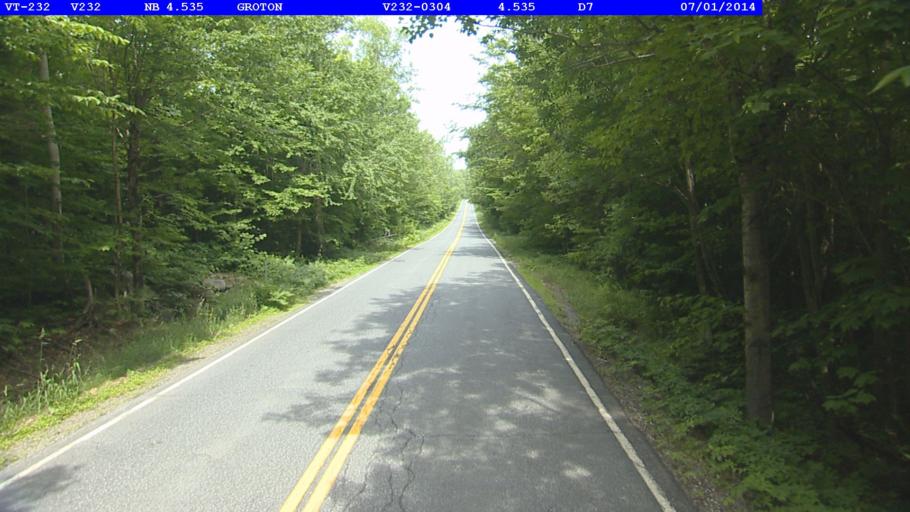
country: US
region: Vermont
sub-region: Washington County
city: Barre
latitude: 44.2675
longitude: -72.2755
